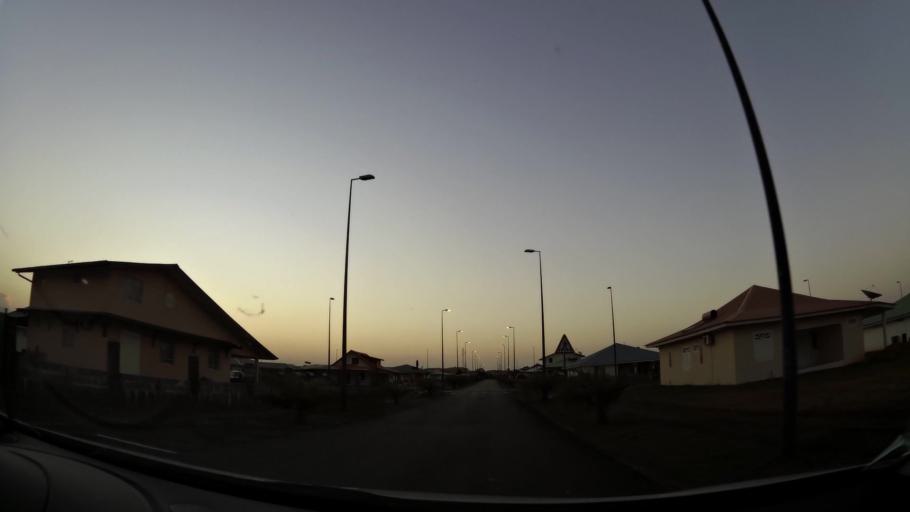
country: GF
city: Macouria
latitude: 4.9238
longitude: -52.4078
